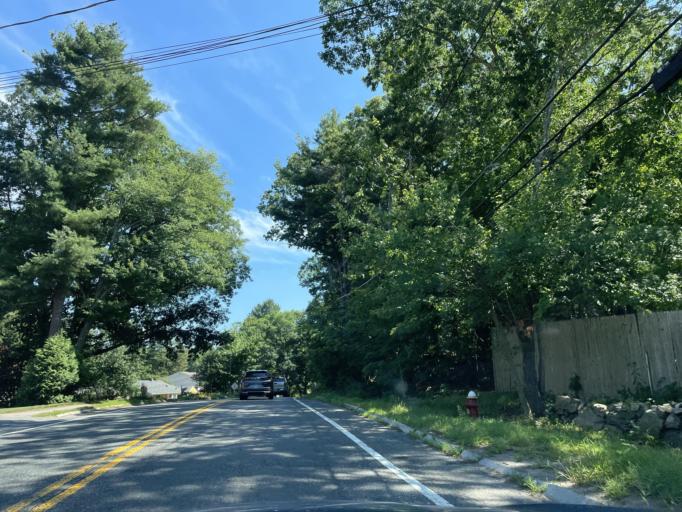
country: US
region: Massachusetts
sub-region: Middlesex County
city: Holliston
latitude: 42.2211
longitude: -71.4278
